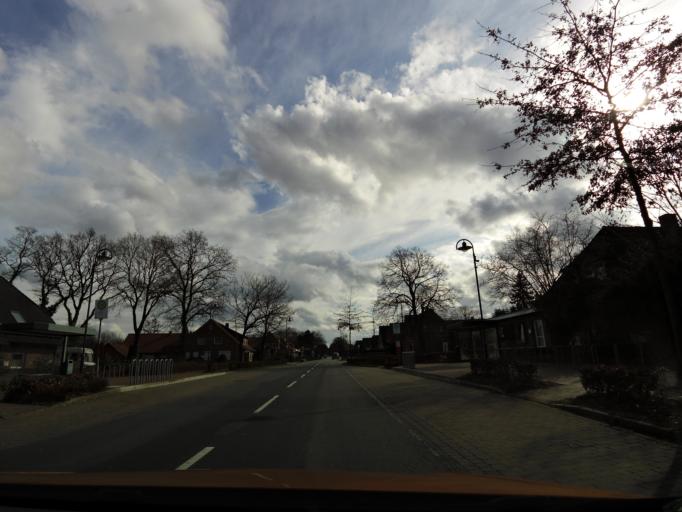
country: DE
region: Lower Saxony
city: Dotlingen
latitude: 52.9775
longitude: 8.3975
